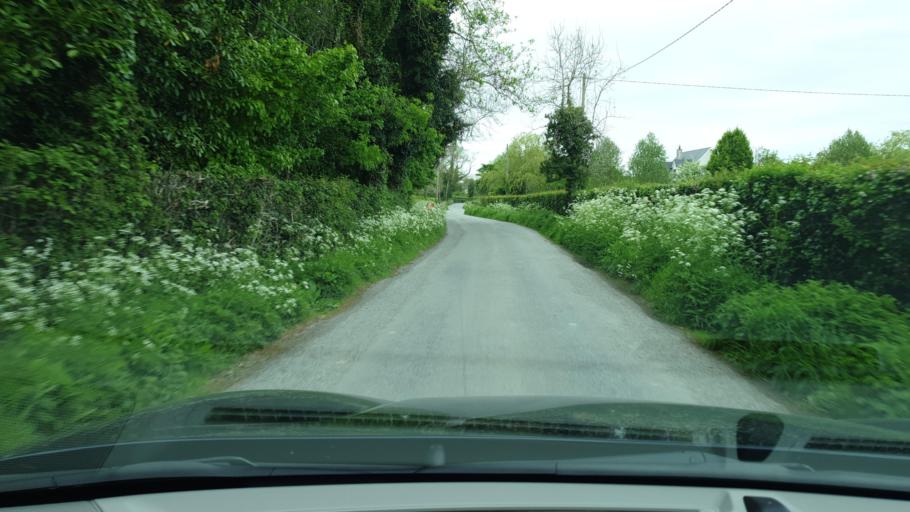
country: IE
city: Confey
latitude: 53.4392
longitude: -6.5254
